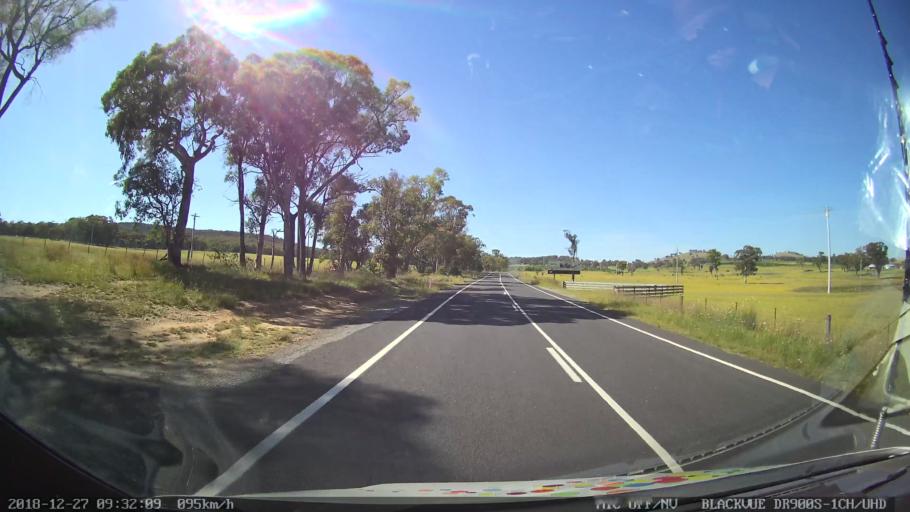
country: AU
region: New South Wales
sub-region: Lithgow
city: Portland
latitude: -33.2032
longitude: 150.0149
